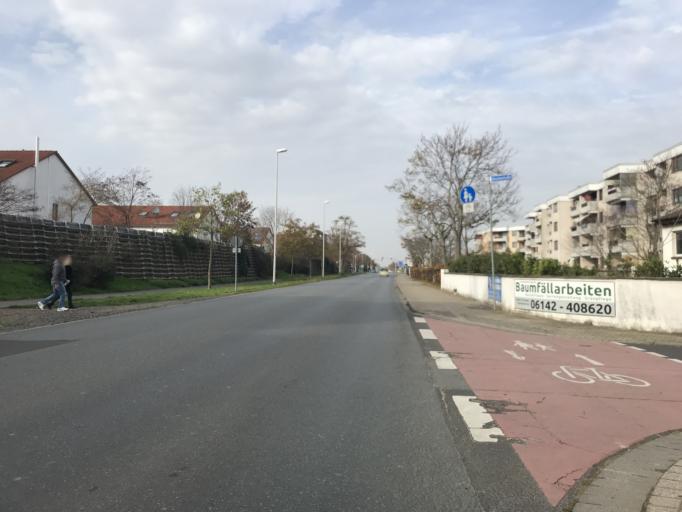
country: DE
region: Hesse
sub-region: Regierungsbezirk Darmstadt
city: Ginsheim-Gustavsburg
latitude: 49.9743
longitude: 8.3422
